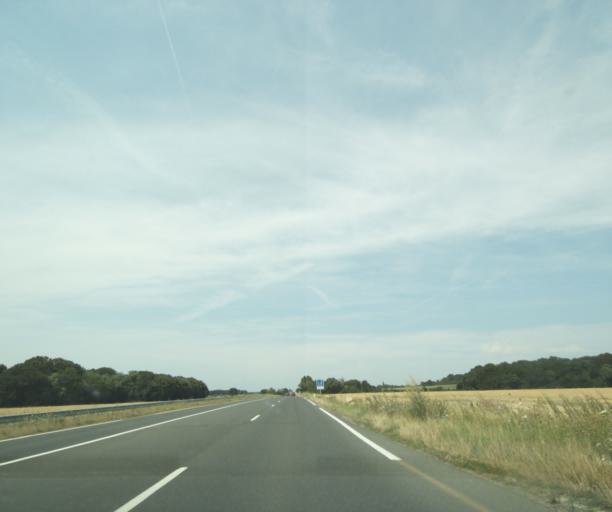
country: FR
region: Centre
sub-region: Departement d'Indre-et-Loire
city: Sorigny
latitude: 47.1817
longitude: 0.6601
